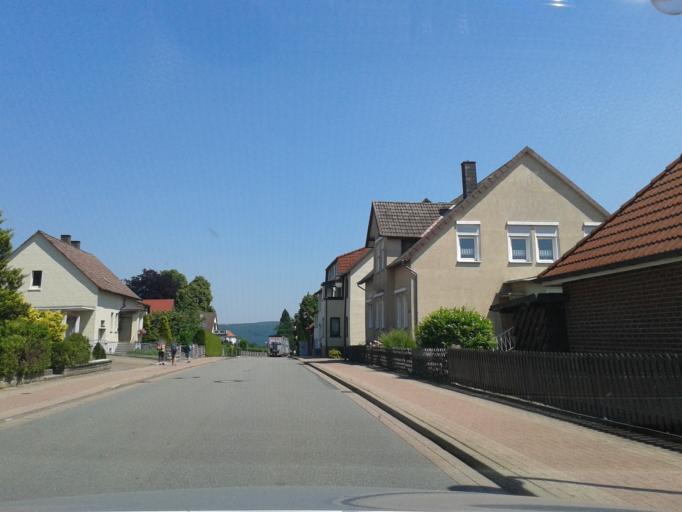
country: DE
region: North Rhine-Westphalia
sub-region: Regierungsbezirk Detmold
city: Lugde
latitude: 51.9750
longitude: 9.1928
